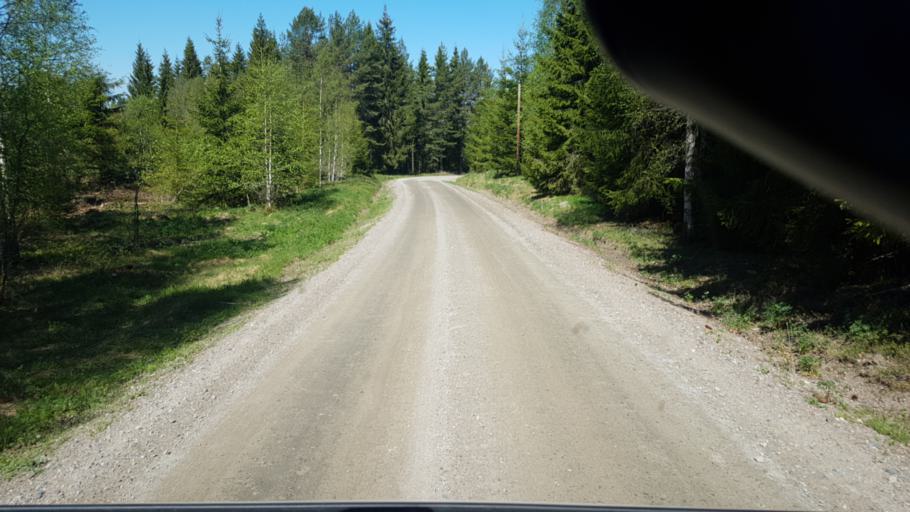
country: SE
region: Vaermland
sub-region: Arvika Kommun
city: Arvika
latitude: 59.8655
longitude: 12.6193
